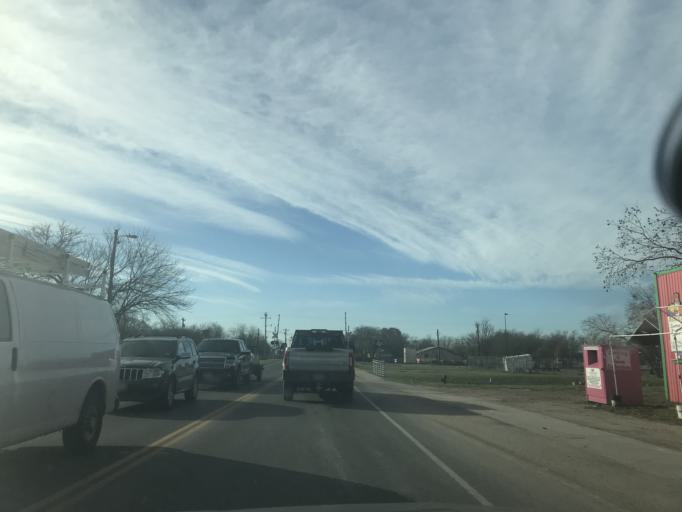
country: US
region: Texas
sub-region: Travis County
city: Manor
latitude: 30.3407
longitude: -97.5578
